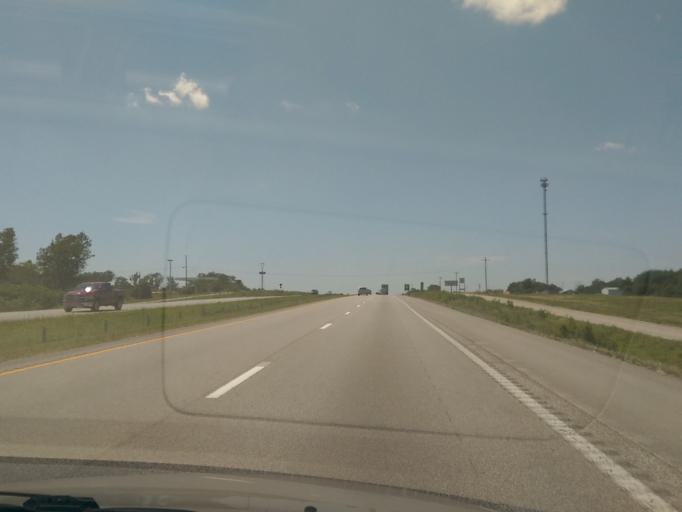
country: US
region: Missouri
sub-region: Saline County
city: Sweet Springs
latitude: 38.9714
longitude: -93.2635
